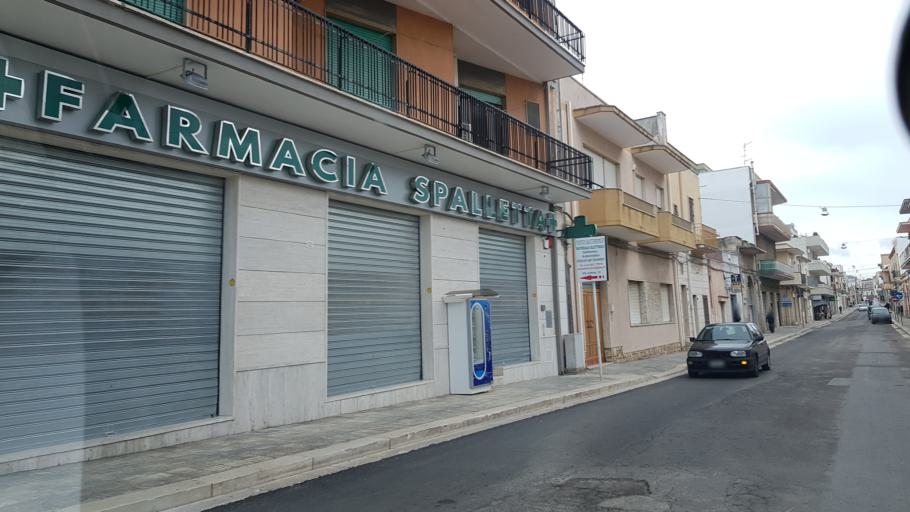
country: IT
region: Apulia
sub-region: Provincia di Brindisi
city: Mesagne
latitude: 40.5639
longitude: 17.8043
